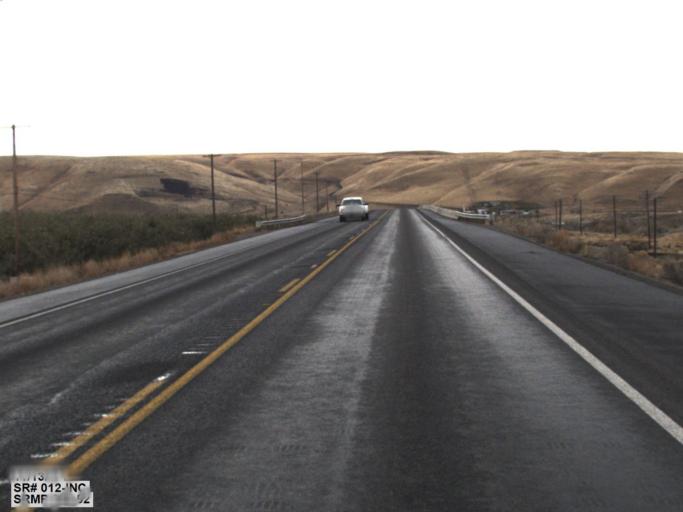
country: US
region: Washington
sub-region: Benton County
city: Finley
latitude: 46.0718
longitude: -118.9079
